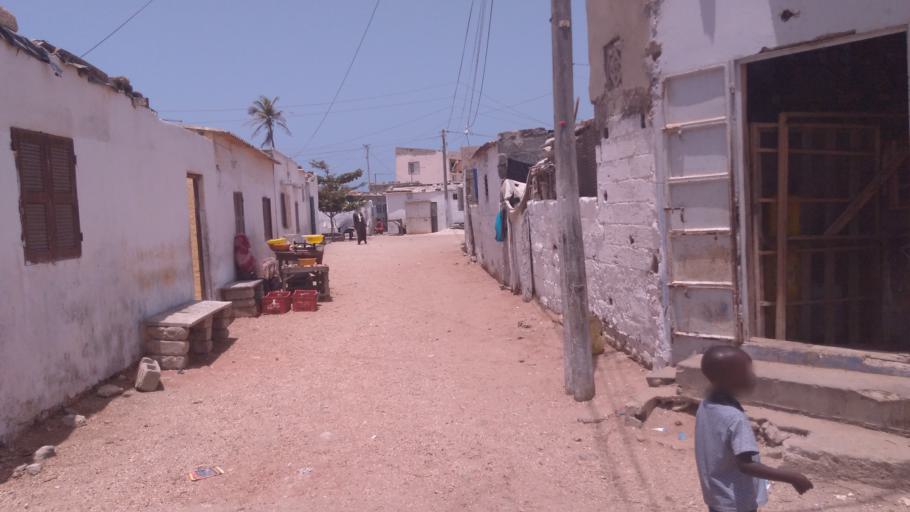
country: SN
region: Dakar
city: Pikine
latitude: 14.6861
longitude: -17.2269
